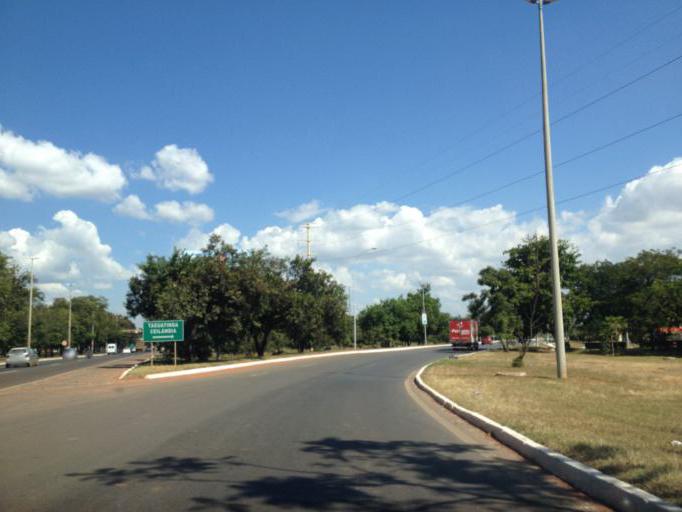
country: BR
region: Federal District
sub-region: Brasilia
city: Brasilia
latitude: -15.8057
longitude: -47.9480
